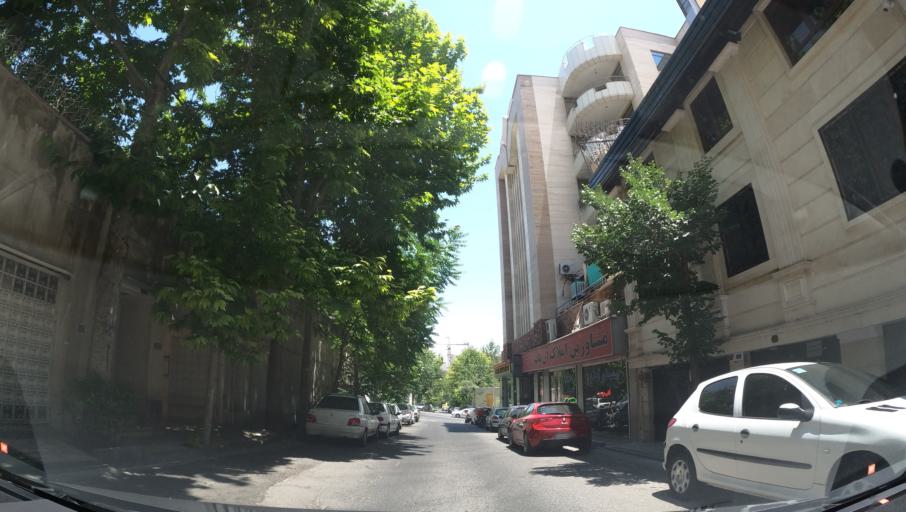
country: IR
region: Tehran
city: Tajrish
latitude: 35.8084
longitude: 51.4003
